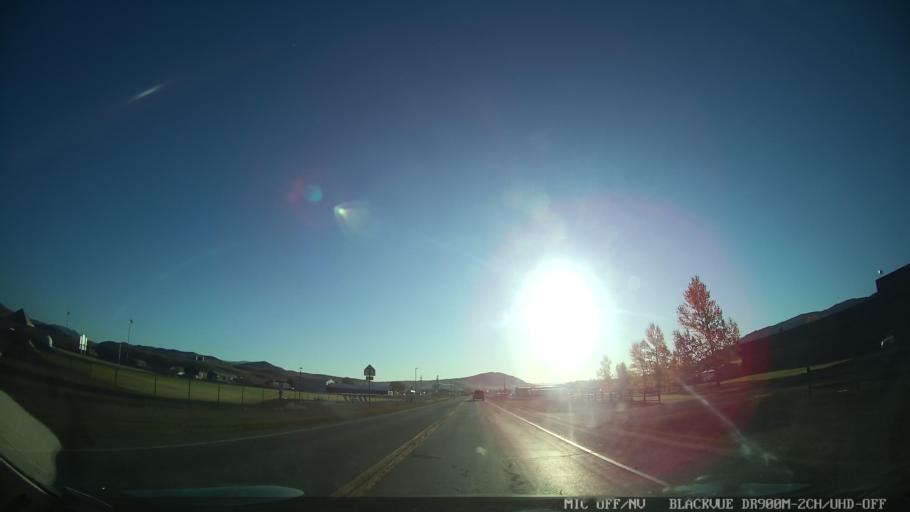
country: US
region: Colorado
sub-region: Grand County
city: Kremmling
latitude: 40.0582
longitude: -106.3788
